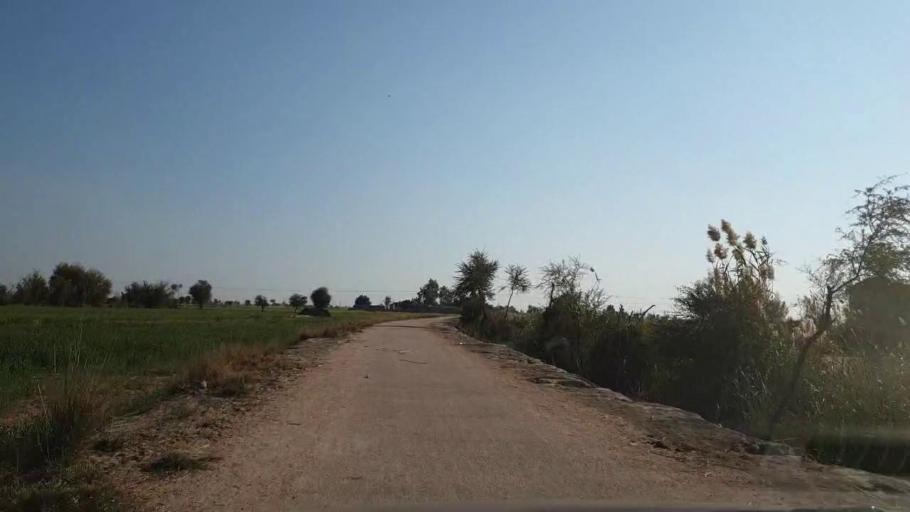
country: PK
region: Sindh
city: Khadro
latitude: 26.1548
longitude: 68.7686
